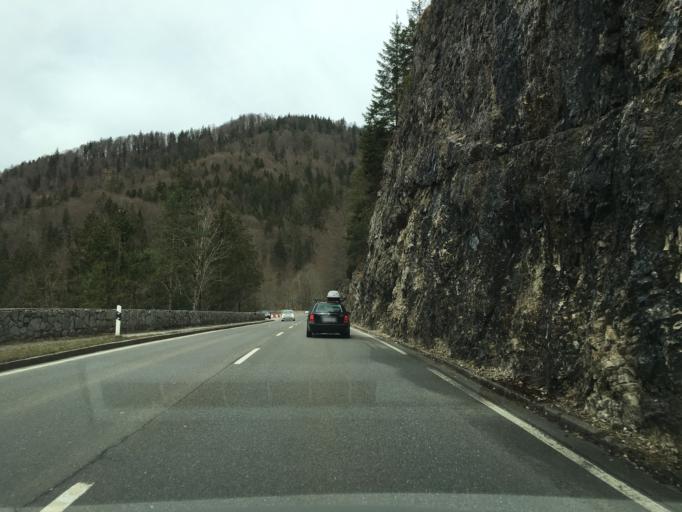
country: DE
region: Bavaria
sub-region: Upper Bavaria
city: Schneizlreuth
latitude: 47.7099
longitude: 12.7931
